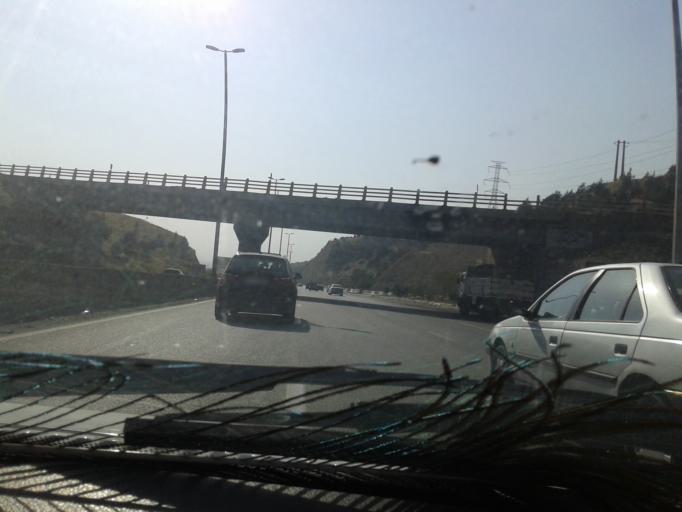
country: IR
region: Tehran
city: Tehran
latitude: 35.7332
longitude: 51.6596
